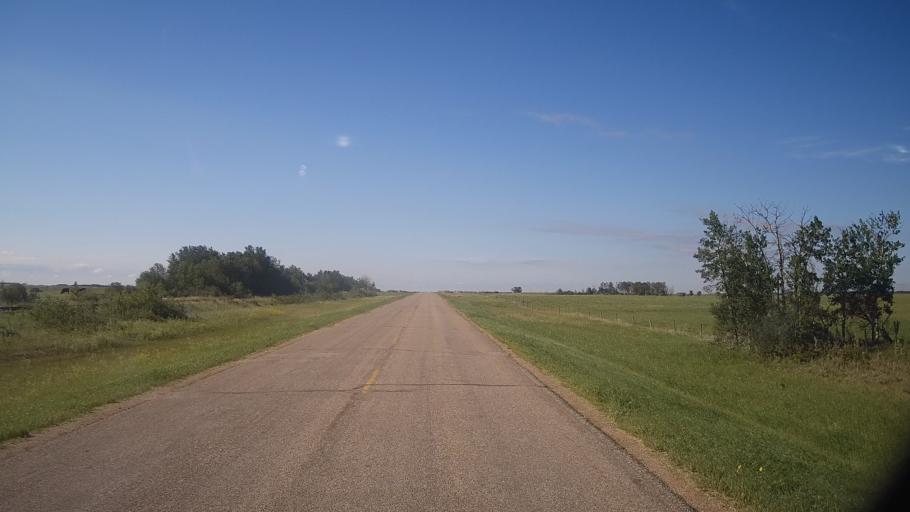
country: CA
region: Saskatchewan
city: Watrous
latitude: 51.7513
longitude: -105.2867
